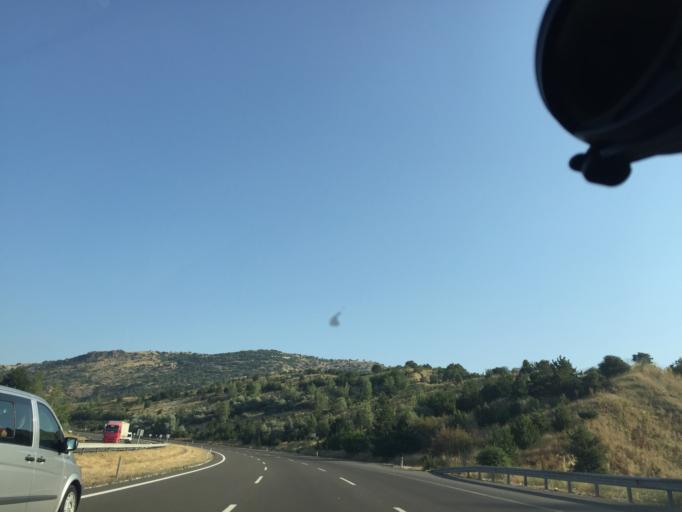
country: TR
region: Ankara
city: Celtikci
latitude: 40.3760
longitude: 32.4711
